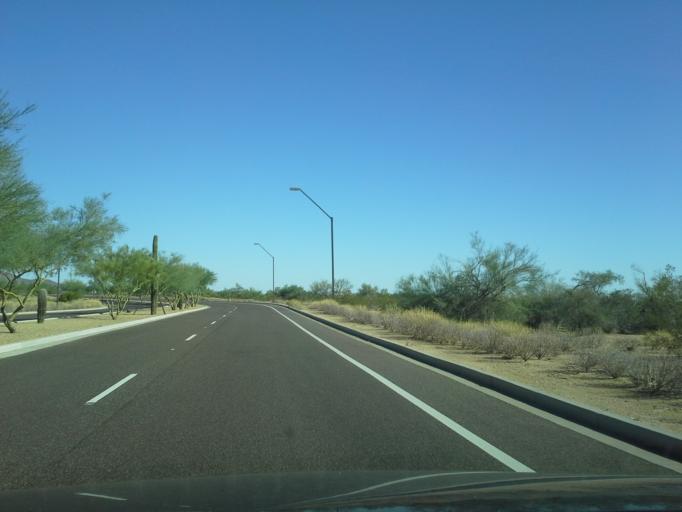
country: US
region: Arizona
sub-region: Maricopa County
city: Paradise Valley
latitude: 33.6631
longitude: -111.9208
